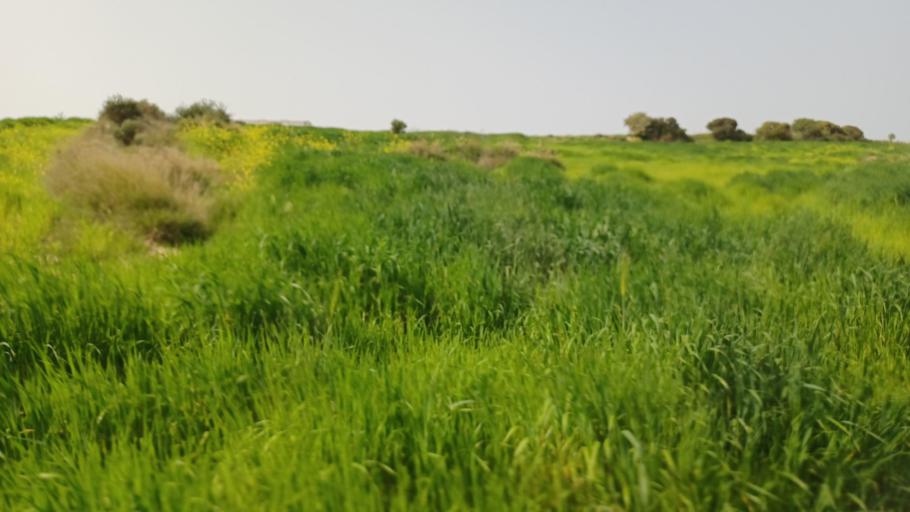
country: CY
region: Pafos
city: Polis
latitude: 35.0082
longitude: 32.3578
